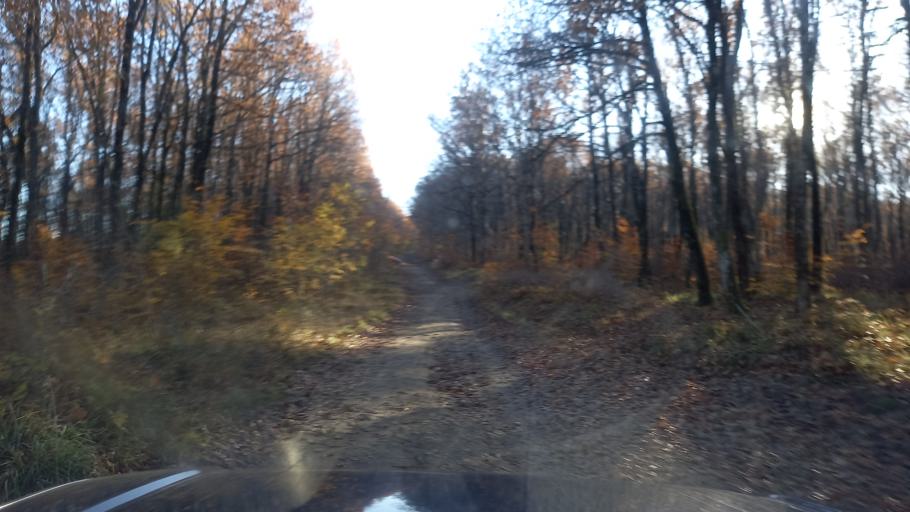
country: RU
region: Krasnodarskiy
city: Goryachiy Klyuch
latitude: 44.6176
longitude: 39.1045
